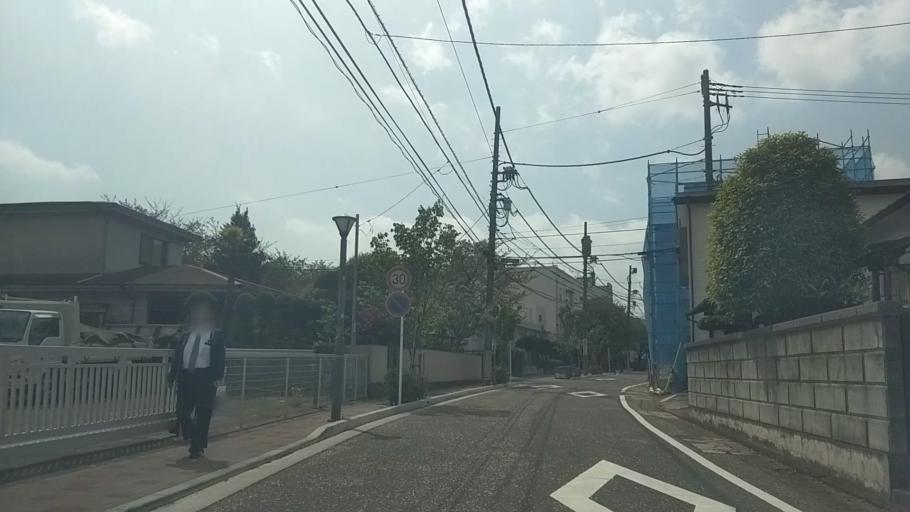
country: JP
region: Kanagawa
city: Yokohama
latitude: 35.3985
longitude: 139.5914
